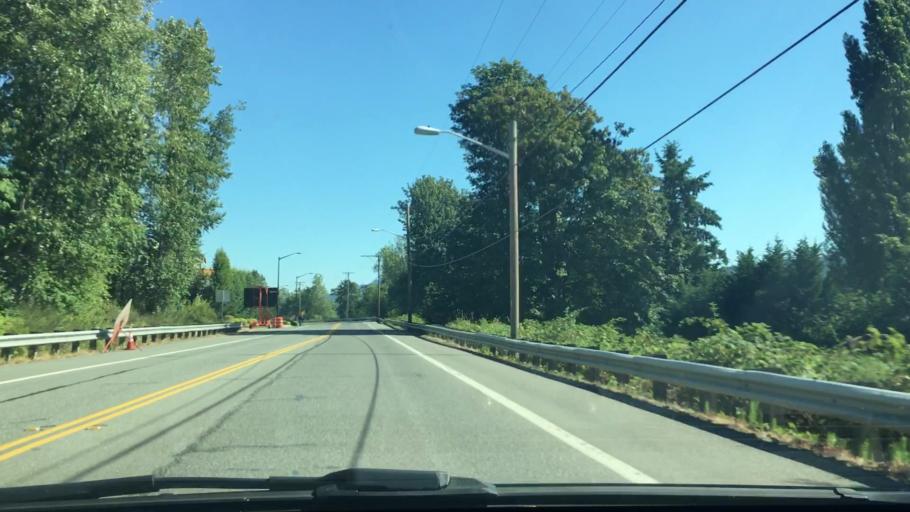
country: US
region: Washington
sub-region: King County
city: West Lake Sammamish
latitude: 47.5776
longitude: -122.0740
